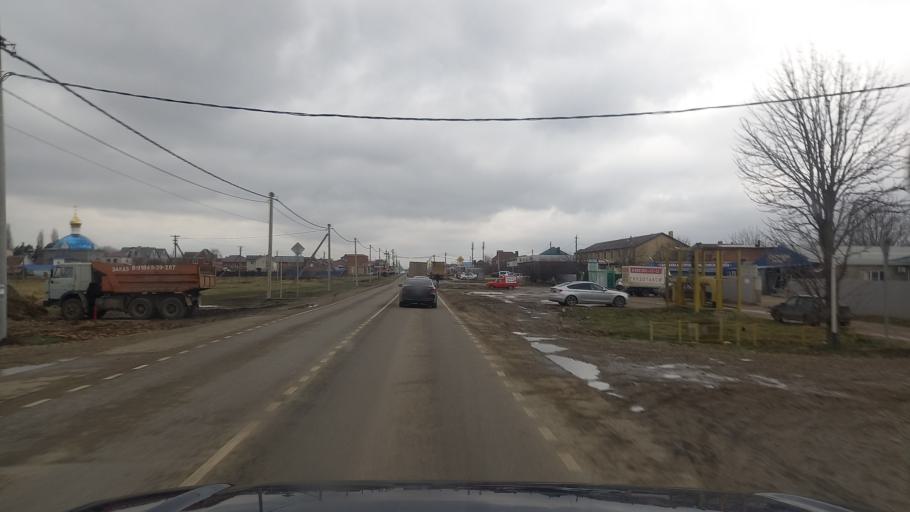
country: RU
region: Krasnodarskiy
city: Pashkovskiy
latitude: 45.0591
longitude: 39.1425
